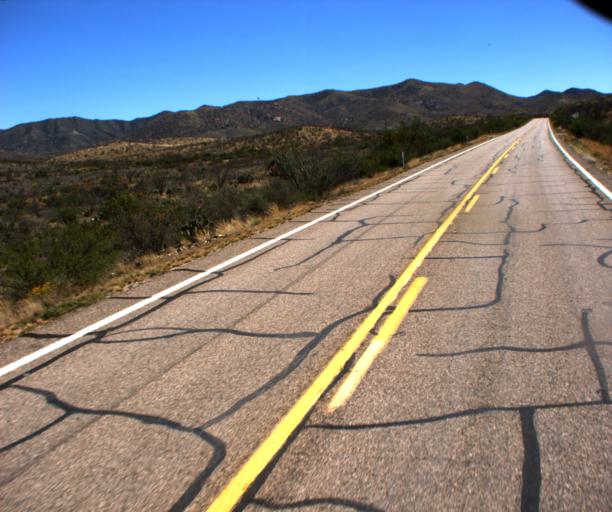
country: US
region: Arizona
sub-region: Pima County
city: Corona de Tucson
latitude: 31.9279
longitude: -110.6580
